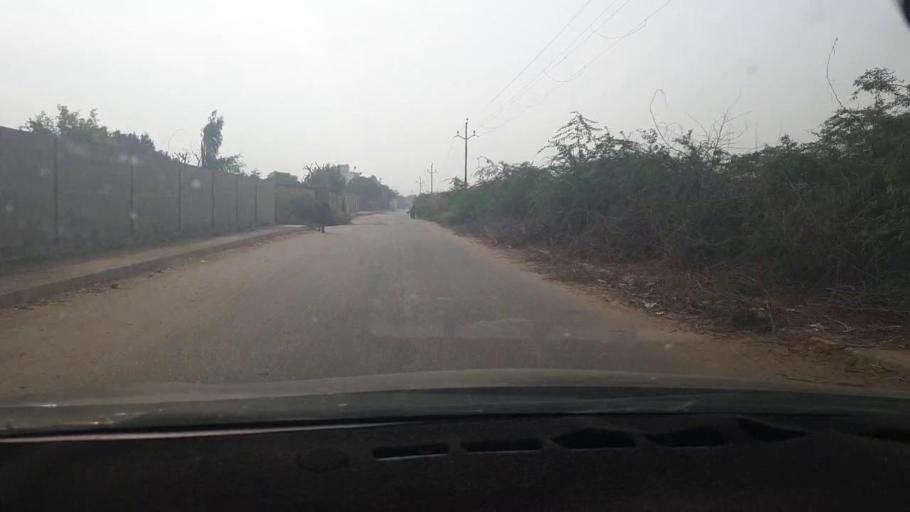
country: PK
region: Sindh
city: Malir Cantonment
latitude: 24.9369
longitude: 67.3345
